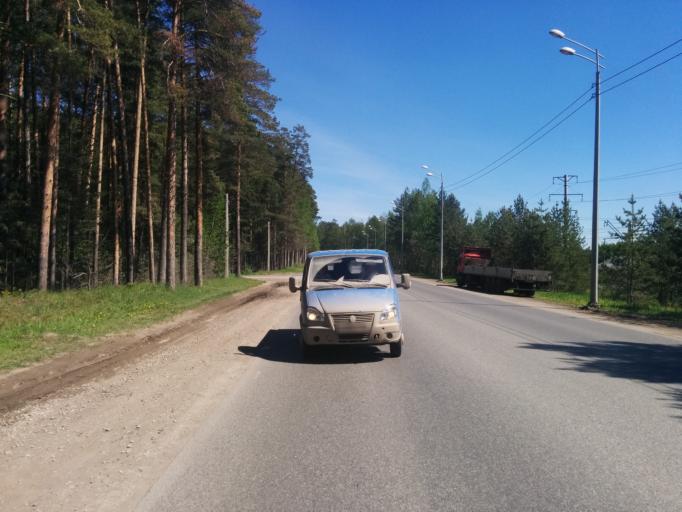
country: RU
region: Perm
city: Perm
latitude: 58.0400
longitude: 56.1728
